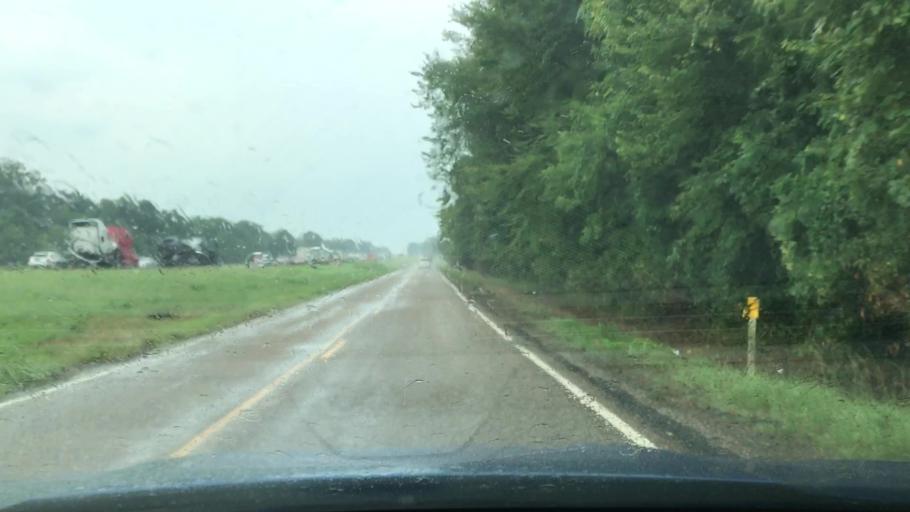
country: US
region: Texas
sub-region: Harrison County
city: Waskom
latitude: 32.4876
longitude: -94.1347
